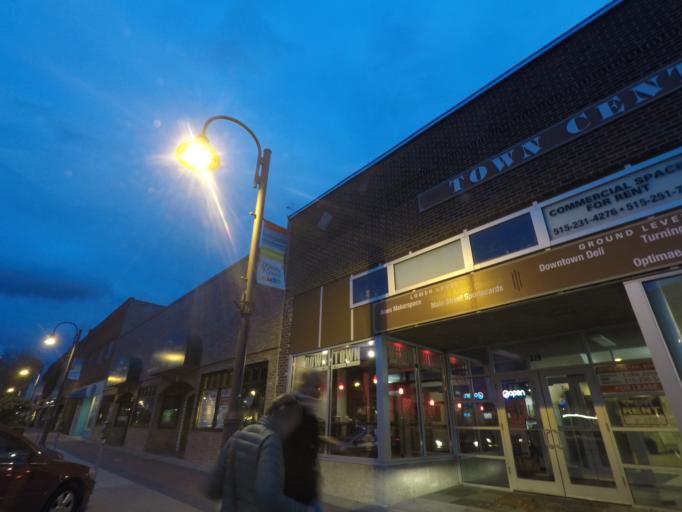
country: US
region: Iowa
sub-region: Story County
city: Ames
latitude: 42.0252
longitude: -93.6149
